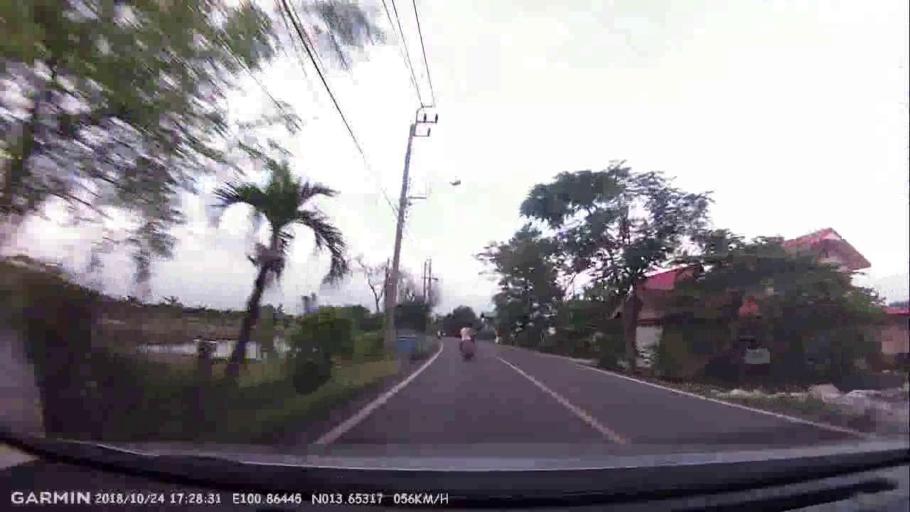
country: TH
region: Samut Prakan
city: Ban Khlong Bang Sao Thong
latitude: 13.6533
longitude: 100.8644
